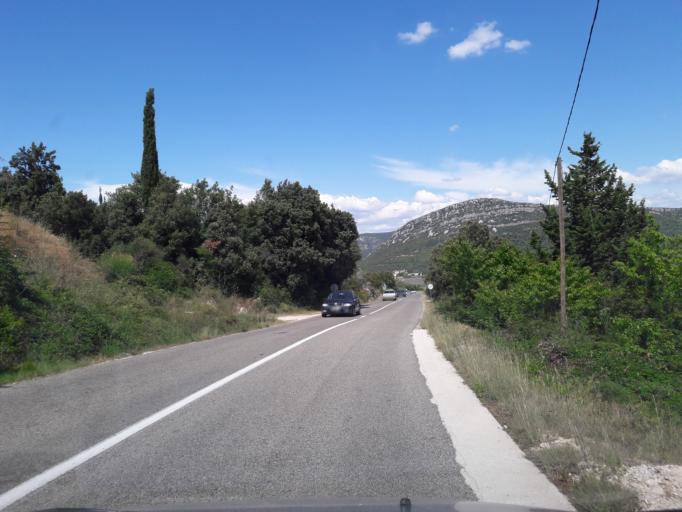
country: HR
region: Dubrovacko-Neretvanska
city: Ston
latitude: 42.8220
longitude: 17.6784
